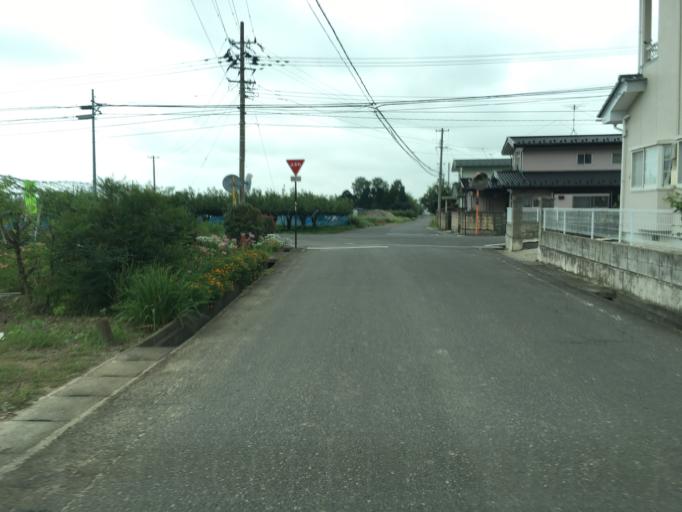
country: JP
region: Fukushima
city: Fukushima-shi
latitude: 37.7763
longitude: 140.3830
